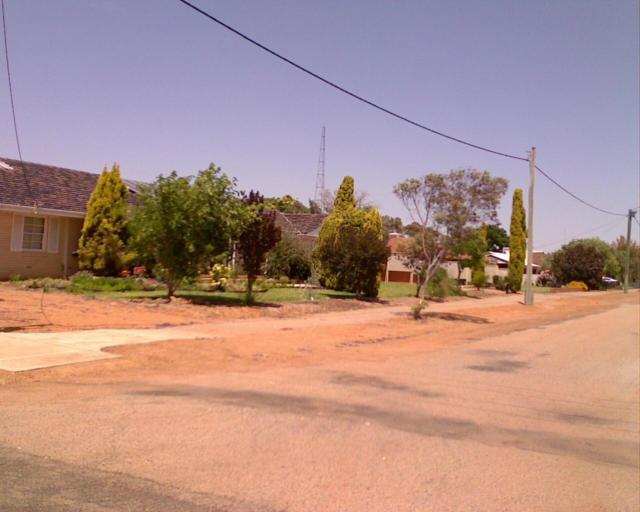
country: AU
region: Western Australia
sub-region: Merredin
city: Merredin
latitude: -30.9178
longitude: 118.2083
